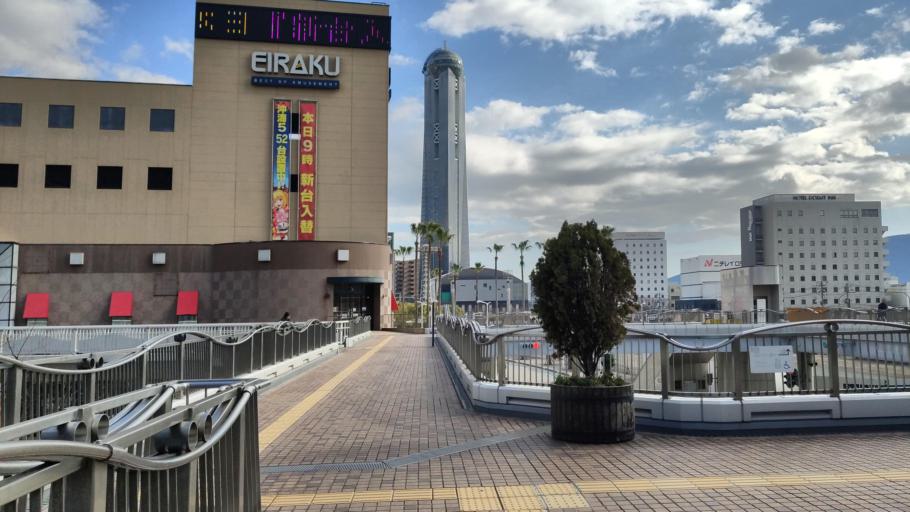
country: JP
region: Yamaguchi
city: Shimonoseki
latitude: 33.9500
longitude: 130.9257
